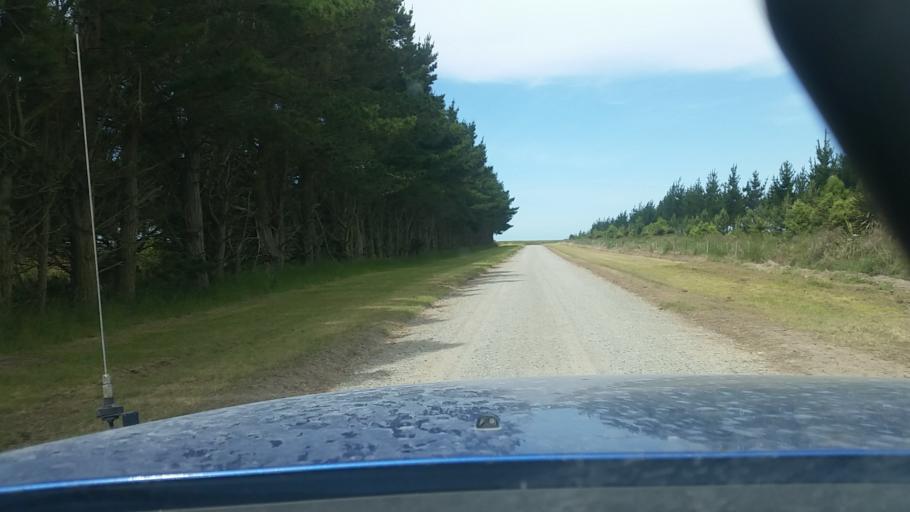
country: NZ
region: Canterbury
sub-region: Ashburton District
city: Tinwald
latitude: -44.0544
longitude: 171.7896
